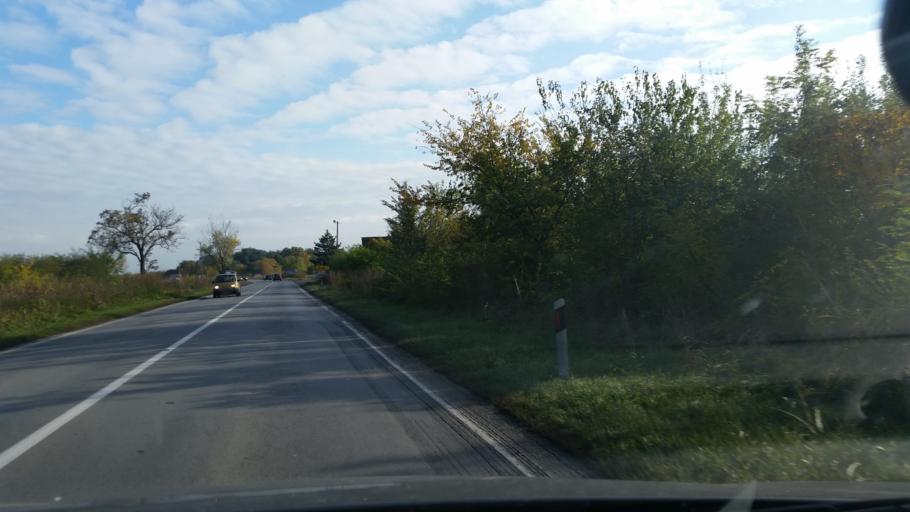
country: RS
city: Ecka
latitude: 45.3339
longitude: 20.4362
